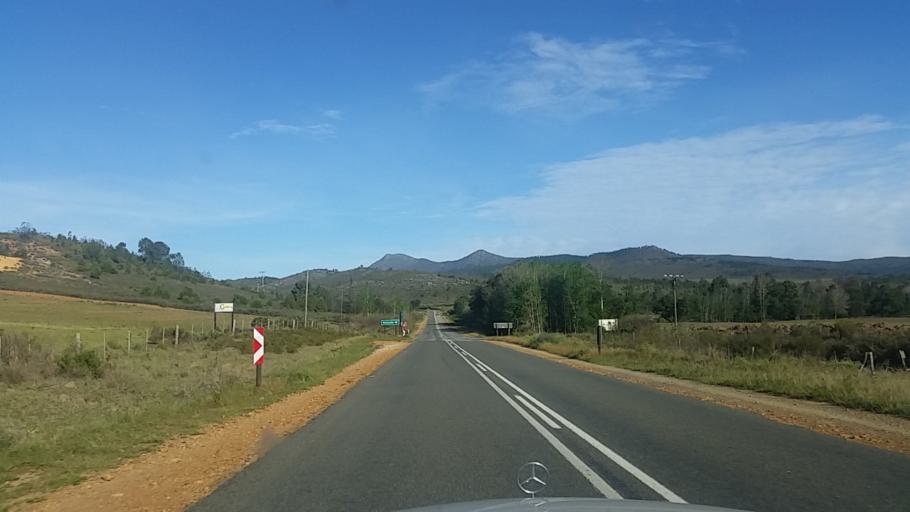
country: ZA
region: Western Cape
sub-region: Eden District Municipality
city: Knysna
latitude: -33.7695
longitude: 22.8957
